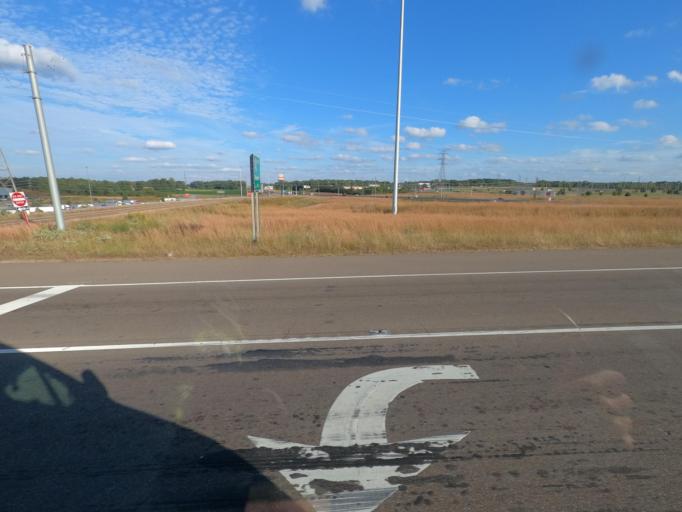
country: US
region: Tennessee
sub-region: Madison County
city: Jackson
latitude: 35.6812
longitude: -88.7798
